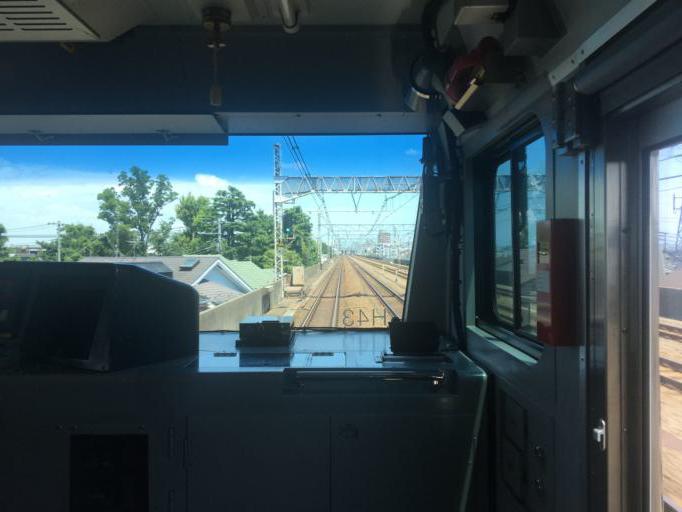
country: JP
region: Tokyo
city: Musashino
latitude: 35.7035
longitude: 139.5893
